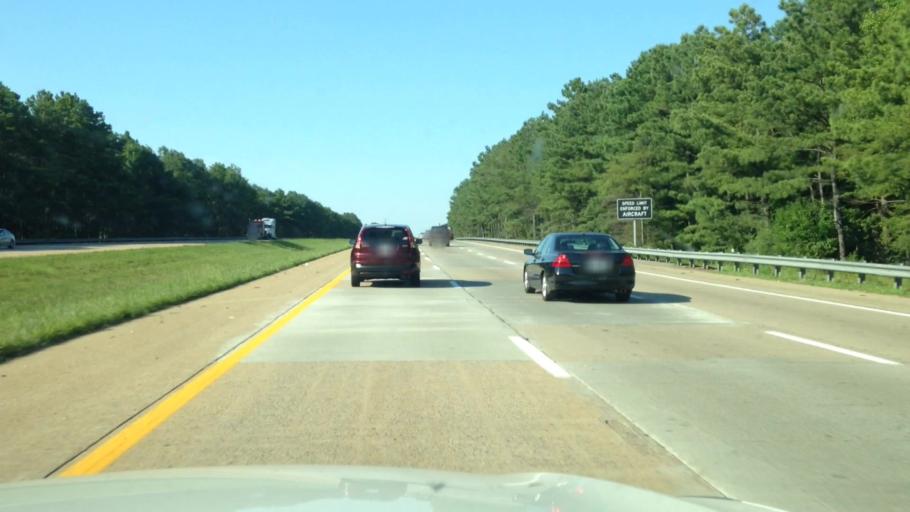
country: US
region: Virginia
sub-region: Henrico County
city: Fort Lee
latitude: 37.4841
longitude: -77.2996
